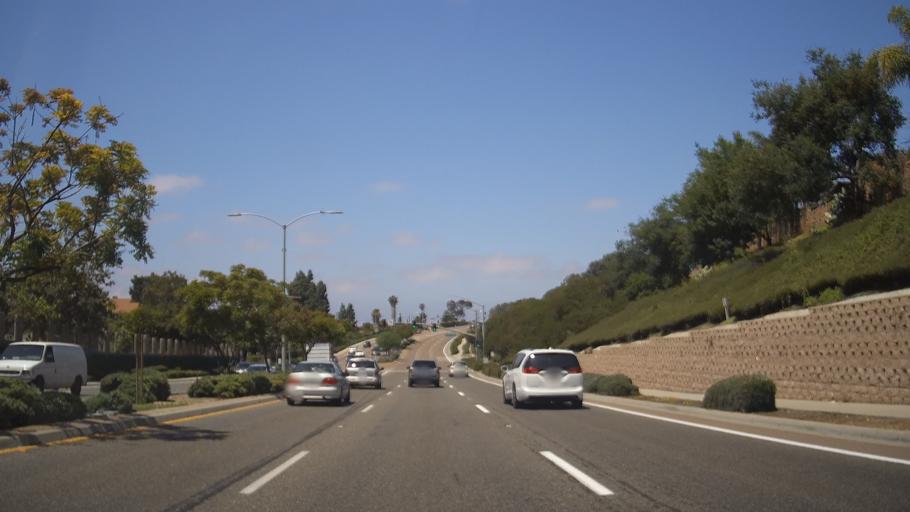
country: US
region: California
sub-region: San Diego County
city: Bonita
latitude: 32.6079
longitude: -117.0294
